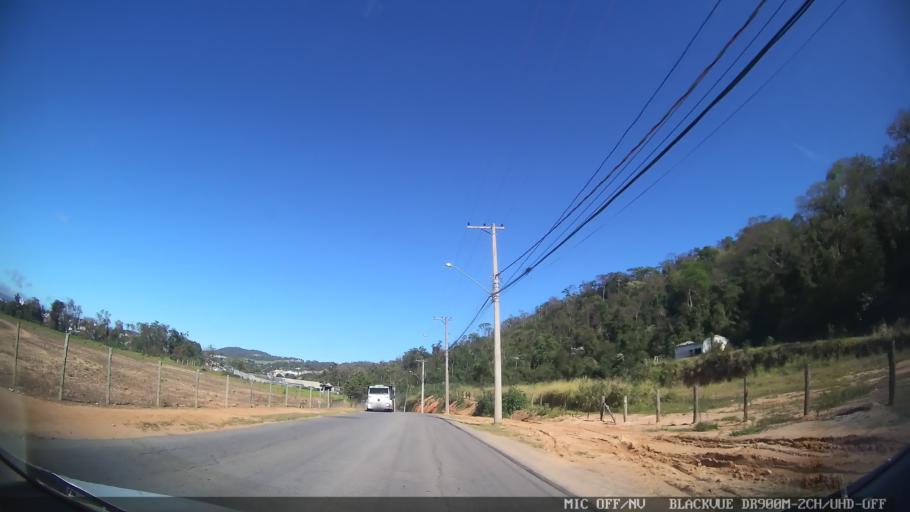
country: BR
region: Sao Paulo
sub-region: Itupeva
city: Itupeva
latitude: -23.1480
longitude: -47.0542
